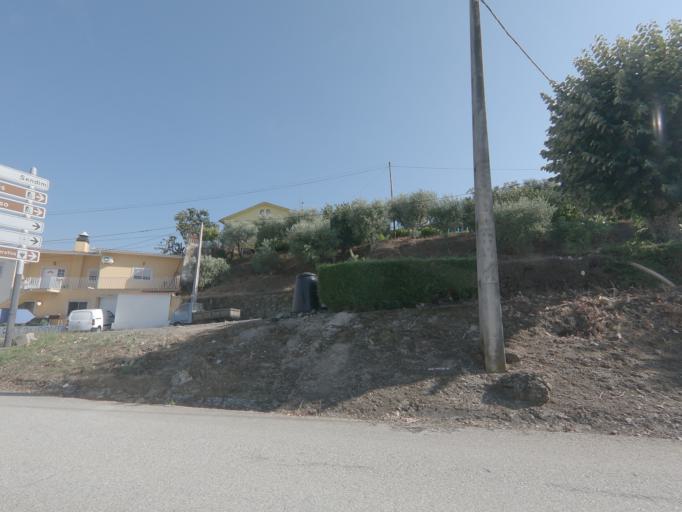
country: PT
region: Viseu
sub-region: Tabuaco
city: Tabuaco
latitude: 41.1158
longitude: -7.5600
